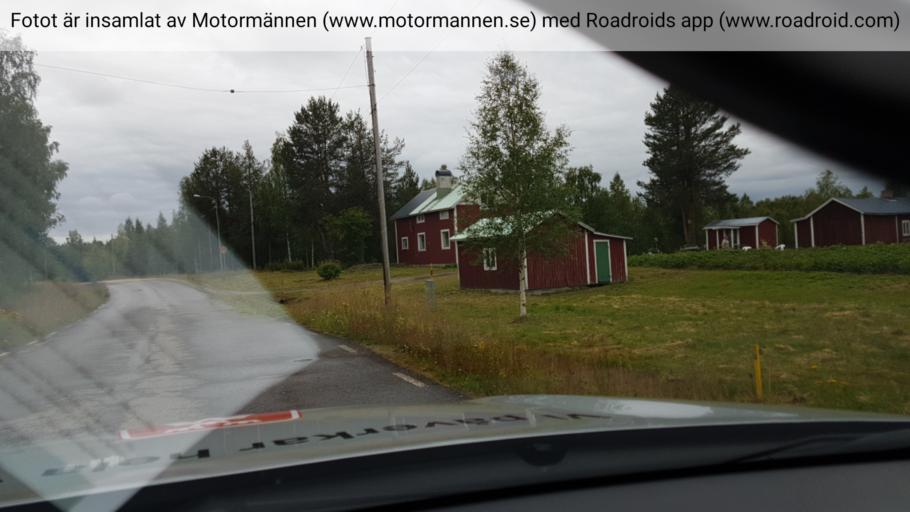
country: SE
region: Norrbotten
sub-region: Pajala Kommun
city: Pajala
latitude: 67.1439
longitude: 22.6495
